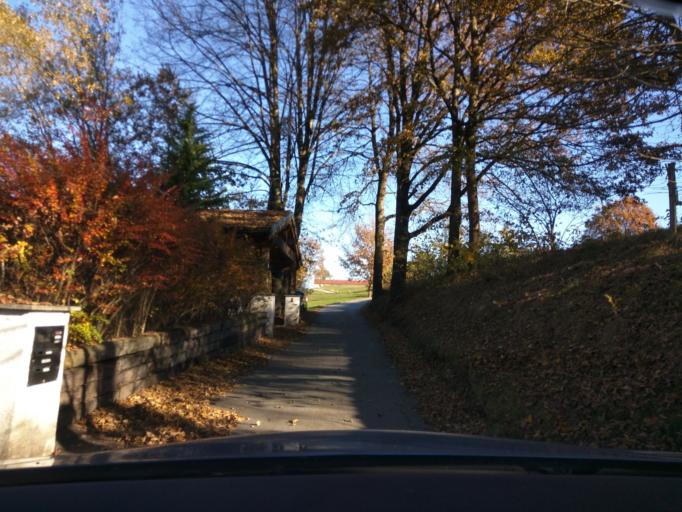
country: DE
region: Bavaria
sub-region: Lower Bavaria
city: Salzweg
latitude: 48.5807
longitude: 13.4841
